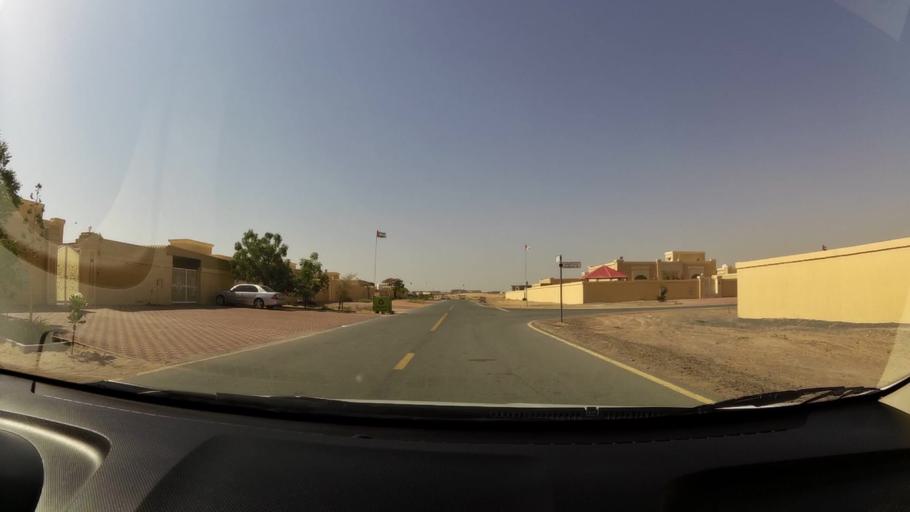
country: AE
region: Umm al Qaywayn
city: Umm al Qaywayn
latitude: 25.4770
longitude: 55.6107
